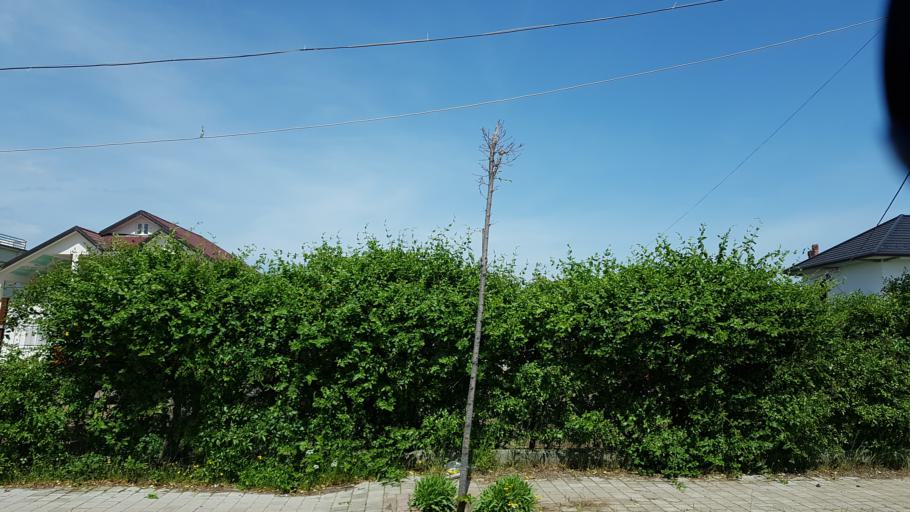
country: AL
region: Shkoder
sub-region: Rrethi i Shkodres
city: Shkoder
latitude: 42.1074
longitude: 19.5617
